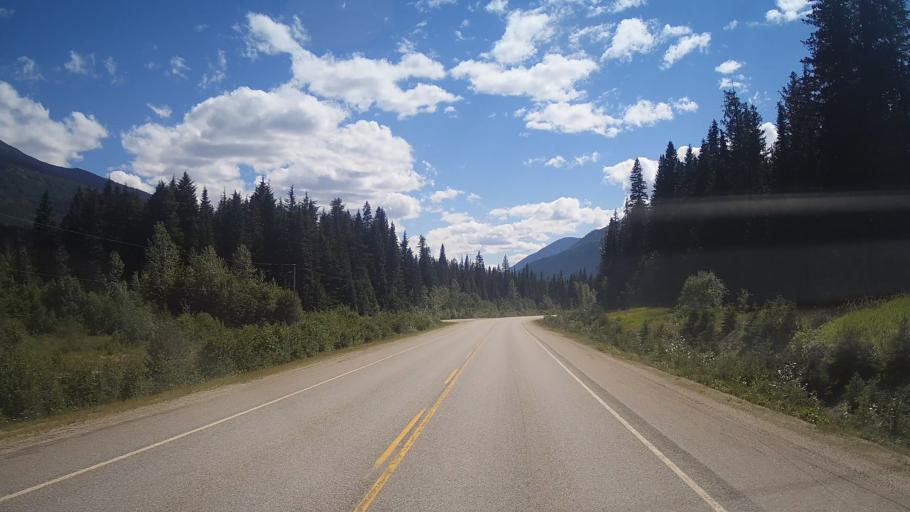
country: CA
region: Alberta
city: Jasper Park Lodge
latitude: 52.5717
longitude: -119.0999
